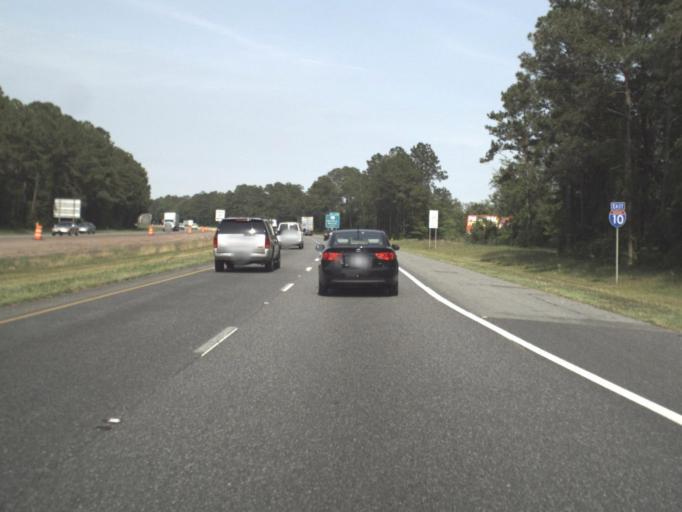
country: US
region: Florida
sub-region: Baker County
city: Macclenny
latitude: 30.2585
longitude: -82.1175
